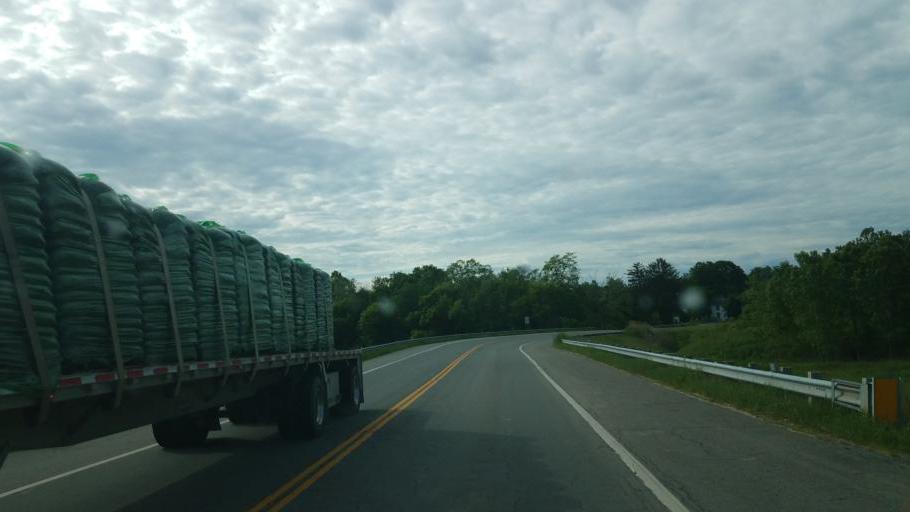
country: US
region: Ohio
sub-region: Medina County
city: Lodi
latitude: 40.9918
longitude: -81.9956
